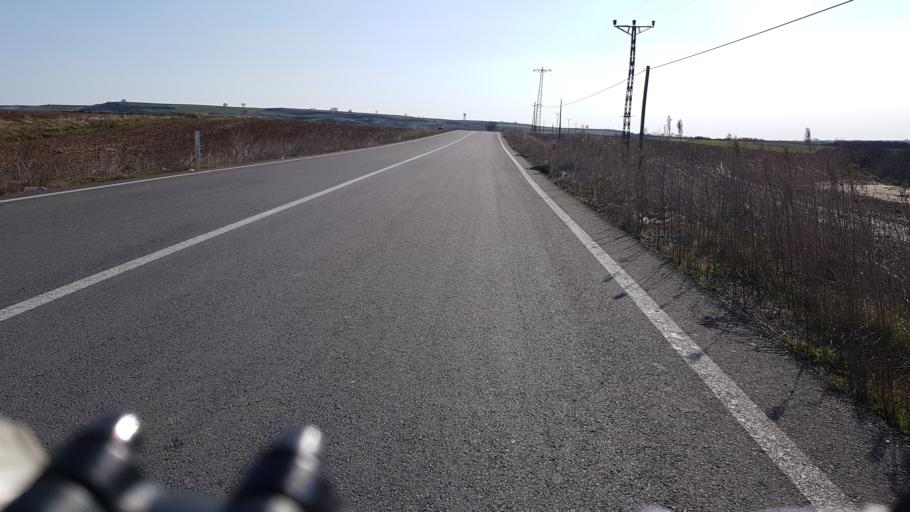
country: TR
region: Tekirdag
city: Saray
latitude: 41.3640
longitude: 27.8572
